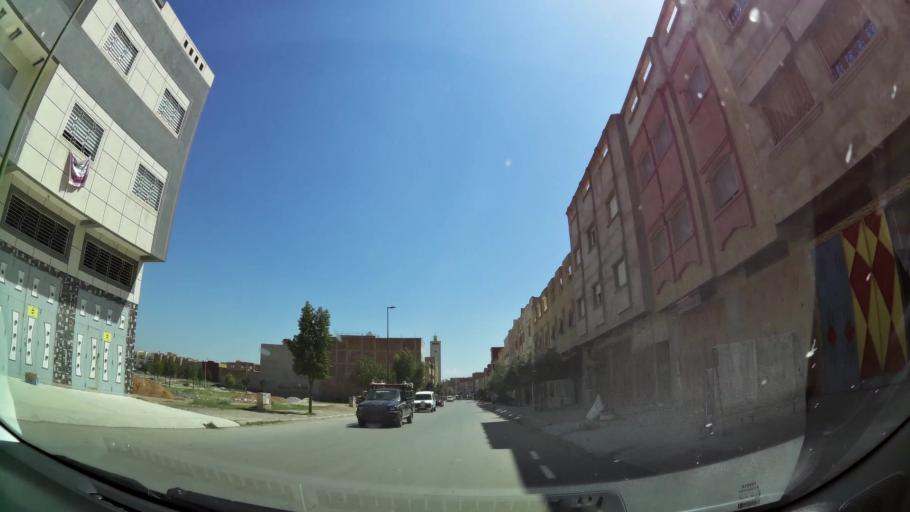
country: MA
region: Oriental
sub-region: Oujda-Angad
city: Oujda
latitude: 34.6881
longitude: -1.9312
